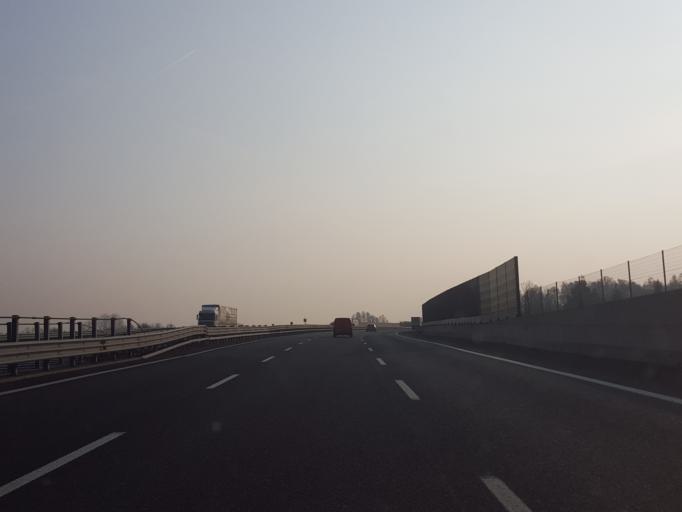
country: IT
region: Veneto
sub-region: Provincia di Venezia
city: Maerne
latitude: 45.5340
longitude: 12.1413
